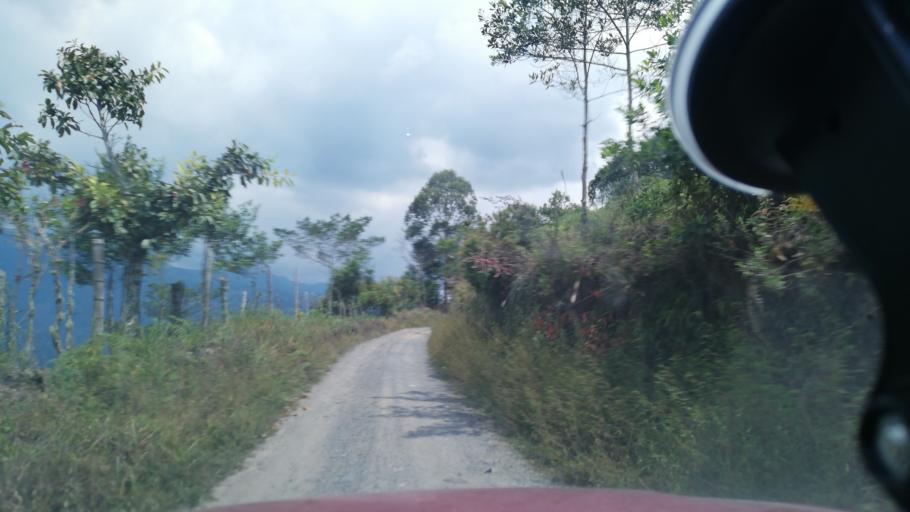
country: CO
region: Cundinamarca
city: Vergara
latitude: 5.1928
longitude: -74.2744
